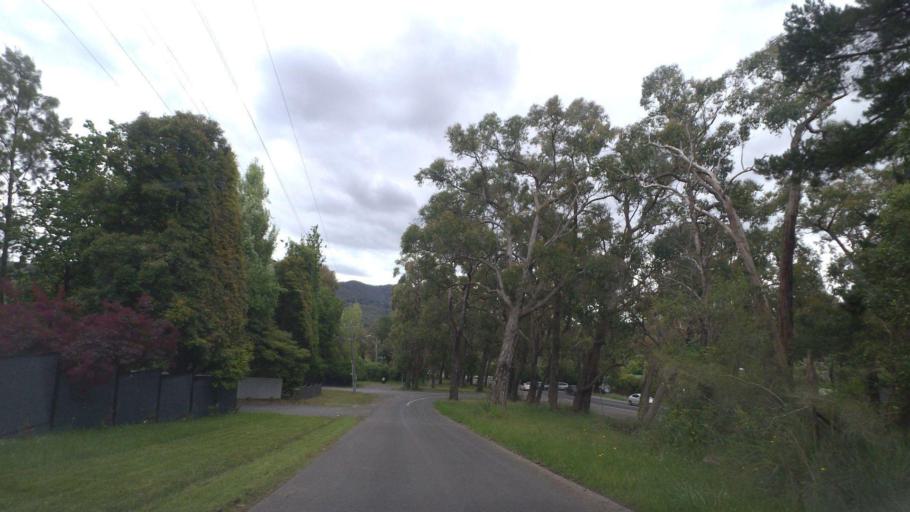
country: AU
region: Victoria
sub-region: Yarra Ranges
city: Mount Evelyn
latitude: -37.7911
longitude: 145.3767
